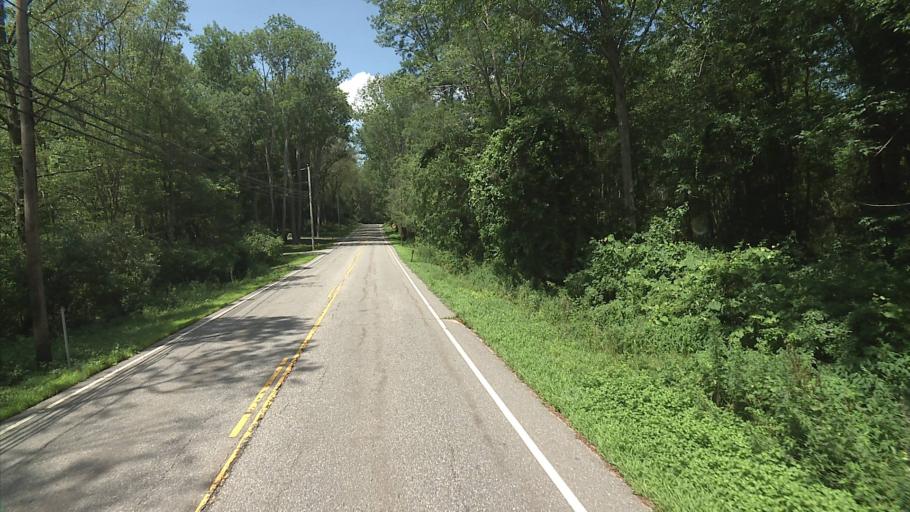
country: US
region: Connecticut
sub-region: Windham County
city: Windham
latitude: 41.6974
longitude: -72.1290
